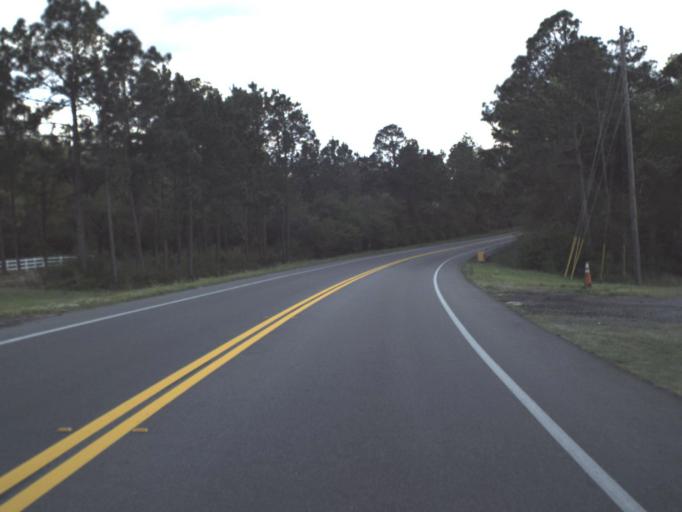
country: US
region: Florida
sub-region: Okaloosa County
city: Crestview
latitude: 30.8818
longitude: -86.5079
